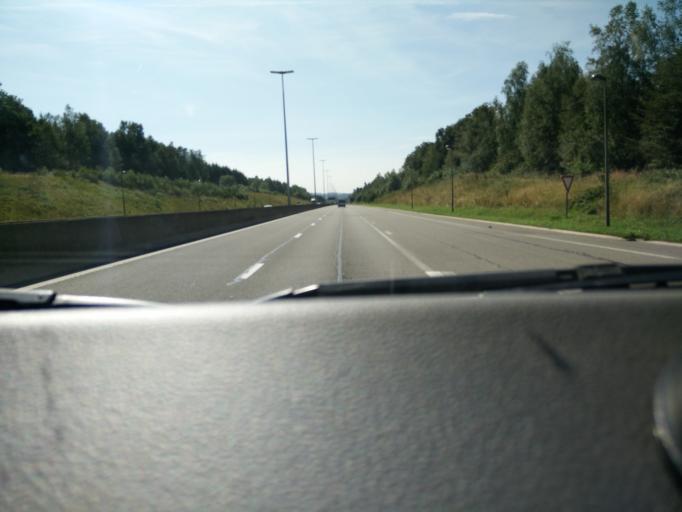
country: BE
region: Wallonia
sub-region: Province du Luxembourg
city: Leglise
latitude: 49.8255
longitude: 5.5135
